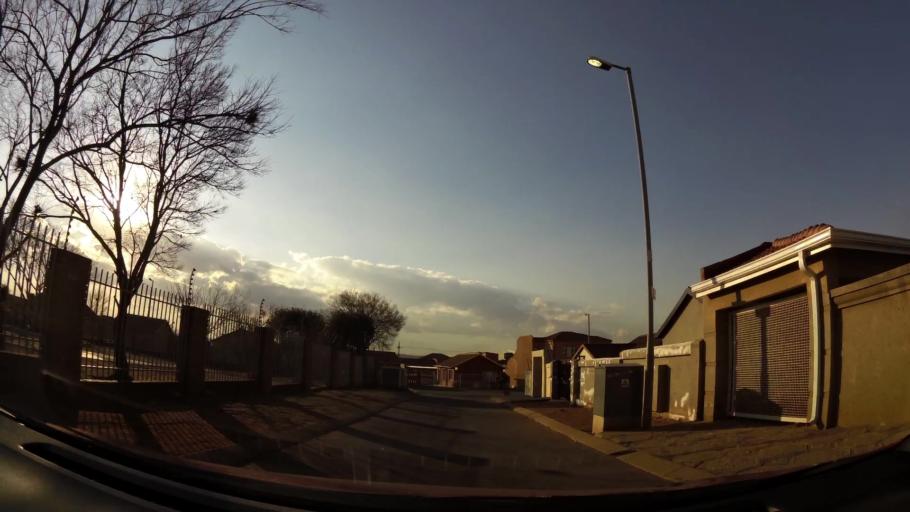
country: ZA
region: Gauteng
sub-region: City of Johannesburg Metropolitan Municipality
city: Soweto
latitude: -26.2307
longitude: 27.8552
